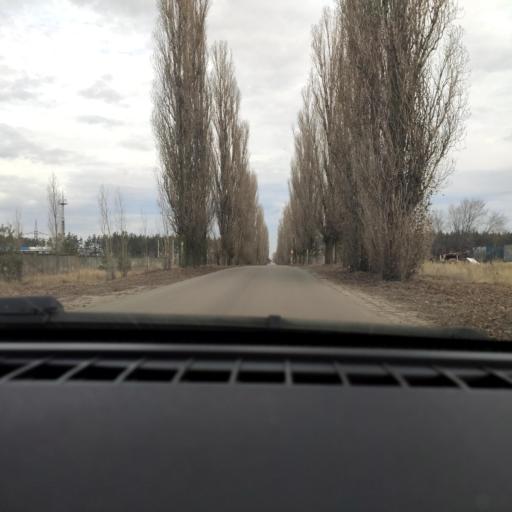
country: RU
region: Voronezj
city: Maslovka
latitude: 51.6016
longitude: 39.2207
